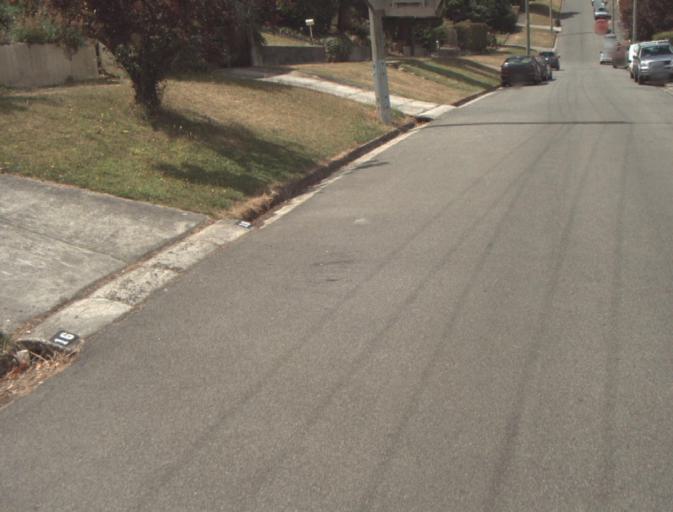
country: AU
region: Tasmania
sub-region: Launceston
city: Launceston
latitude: -41.4359
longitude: 147.1130
